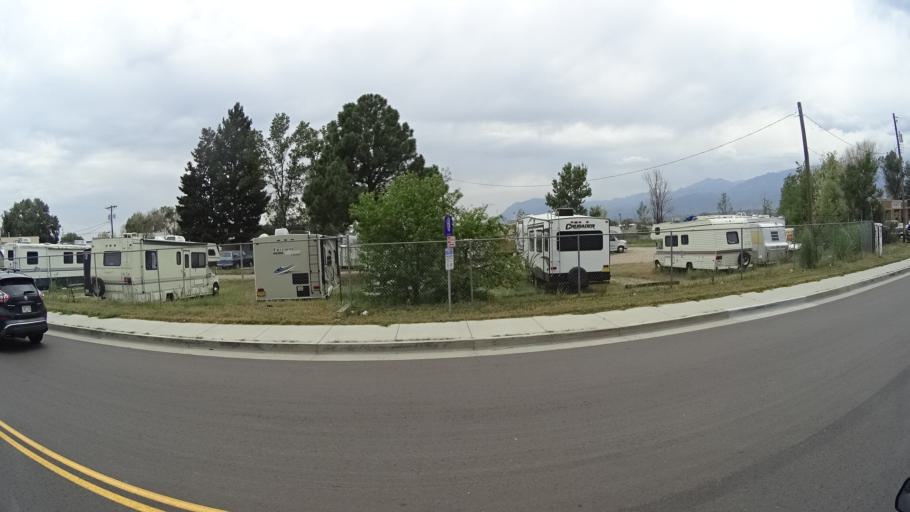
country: US
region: Colorado
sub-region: El Paso County
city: Colorado Springs
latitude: 38.8895
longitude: -104.8150
